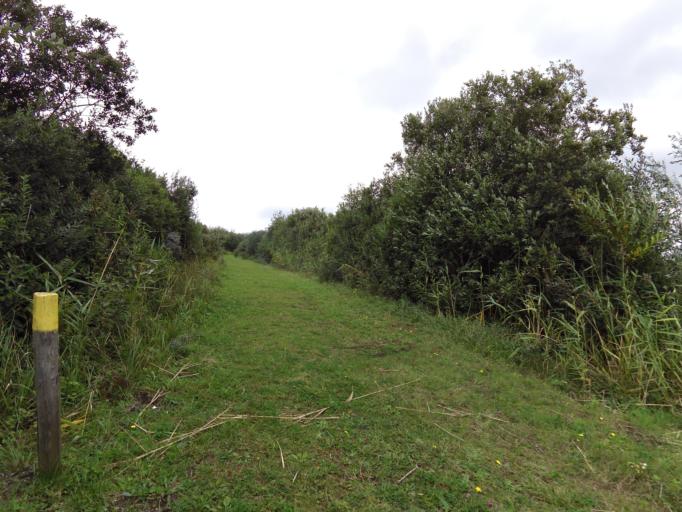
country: NL
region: South Holland
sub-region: Gemeente Goeree-Overflakkee
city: Dirksland
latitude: 51.7610
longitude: 4.0363
